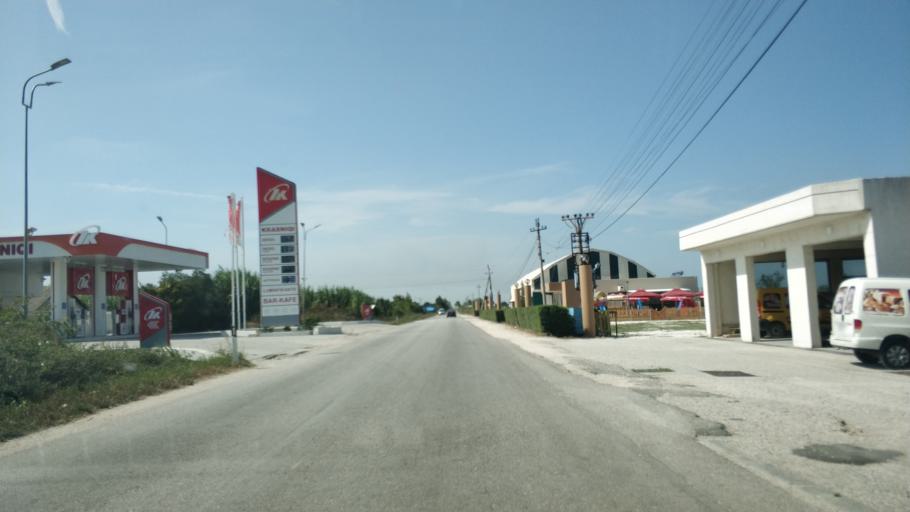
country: AL
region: Fier
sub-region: Rrethi i Fierit
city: Dermenas
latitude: 40.7378
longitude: 19.5173
